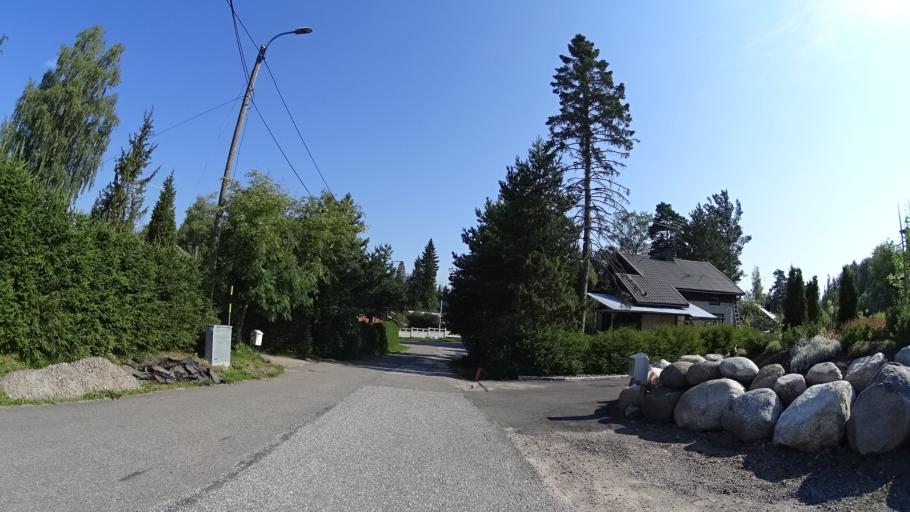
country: FI
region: Uusimaa
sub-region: Helsinki
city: Kerava
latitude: 60.3287
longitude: 25.1078
